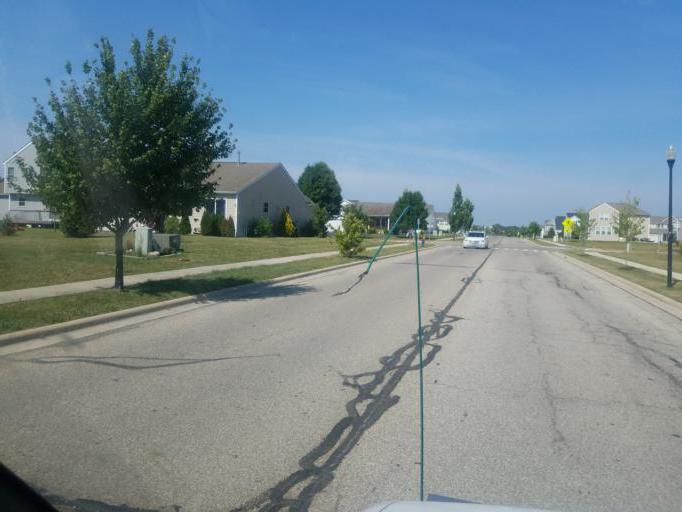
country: US
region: Ohio
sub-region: Union County
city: Marysville
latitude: 40.2688
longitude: -83.3786
